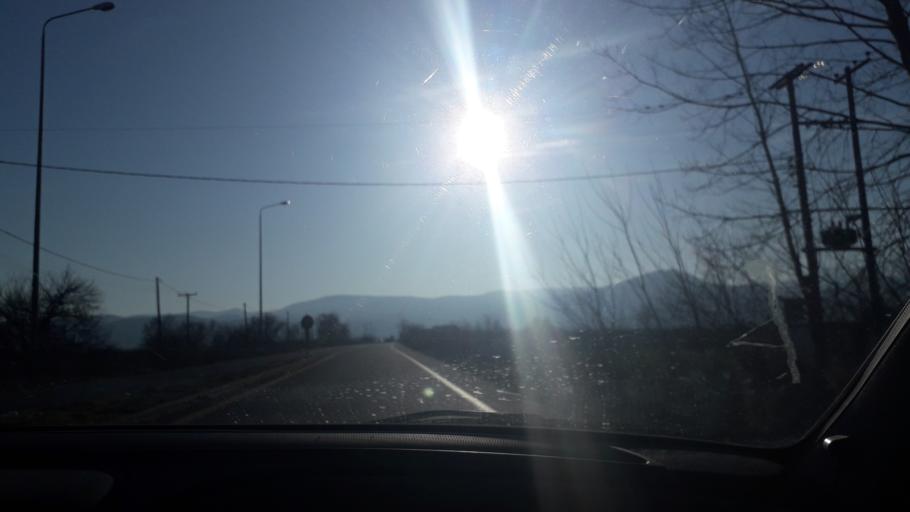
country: GR
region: Central Macedonia
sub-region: Nomos Pellis
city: Apsalos
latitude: 40.9141
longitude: 22.0742
